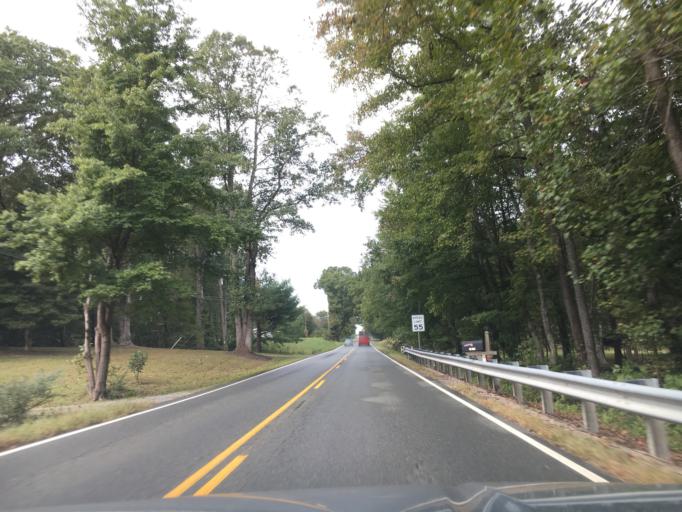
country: US
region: Virginia
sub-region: Goochland County
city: Goochland
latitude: 37.7459
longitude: -77.8527
